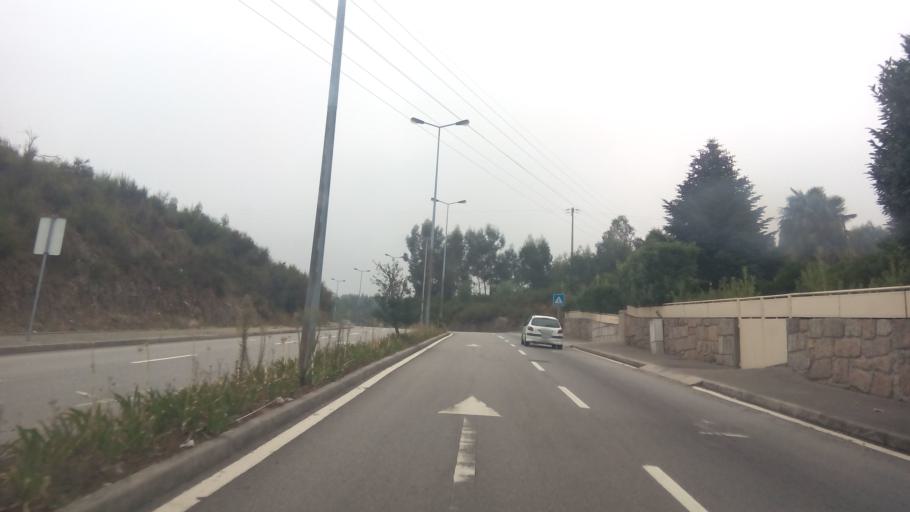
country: PT
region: Porto
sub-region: Paredes
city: Baltar
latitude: 41.1916
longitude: -8.4029
